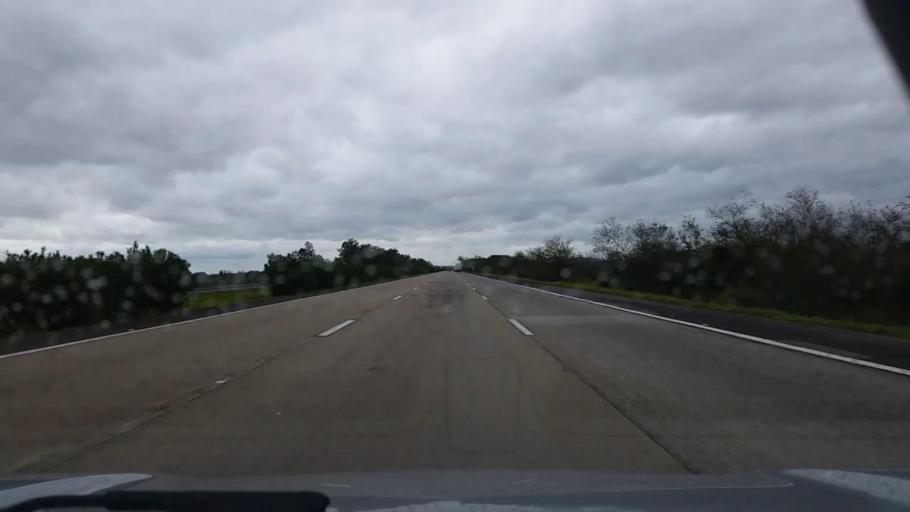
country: BR
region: Rio Grande do Sul
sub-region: Rolante
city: Rolante
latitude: -29.8863
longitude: -50.6418
